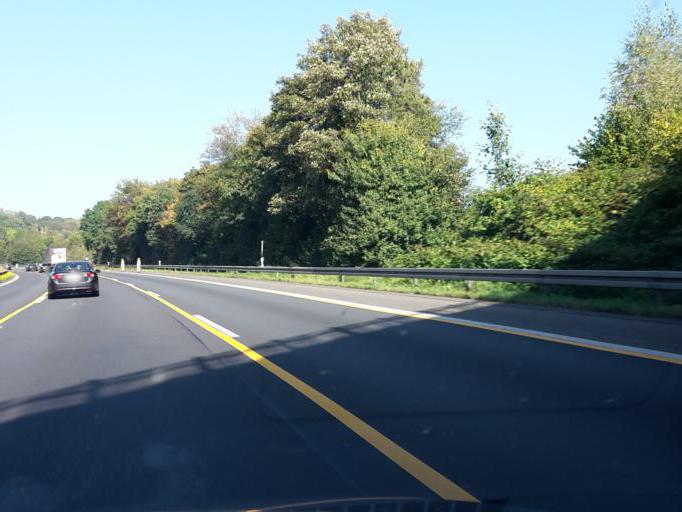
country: DE
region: North Rhine-Westphalia
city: Lohmar
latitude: 50.8503
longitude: 7.2143
